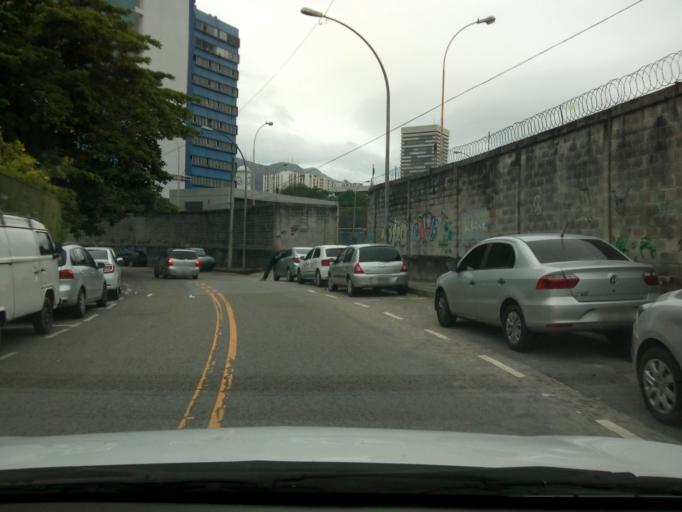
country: BR
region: Rio de Janeiro
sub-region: Rio De Janeiro
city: Rio de Janeiro
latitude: -22.9063
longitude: -43.1990
